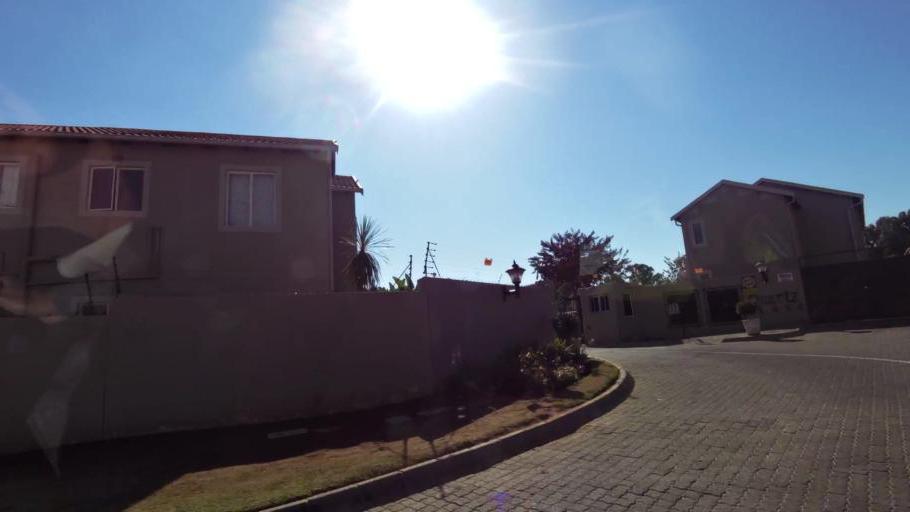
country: ZA
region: Gauteng
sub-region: City of Johannesburg Metropolitan Municipality
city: Johannesburg
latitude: -26.2508
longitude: 27.9932
